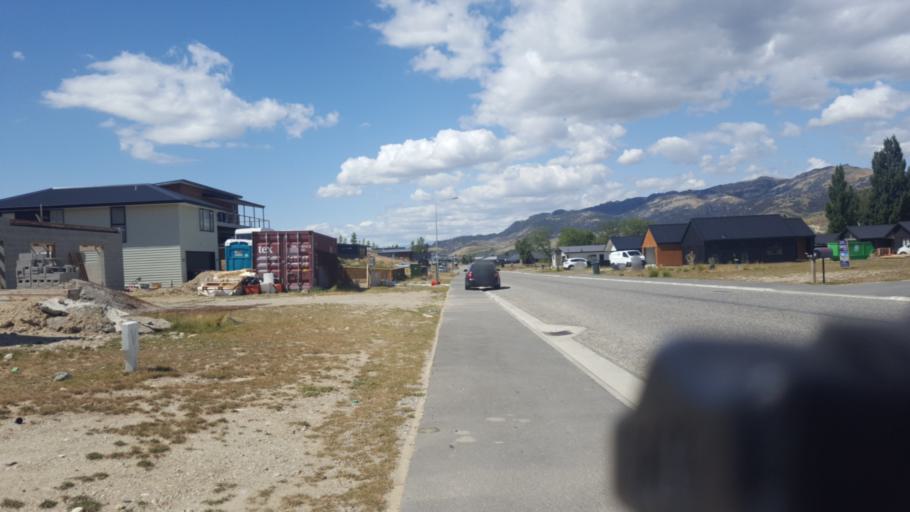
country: NZ
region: Otago
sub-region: Queenstown-Lakes District
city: Wanaka
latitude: -44.9756
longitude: 169.2388
